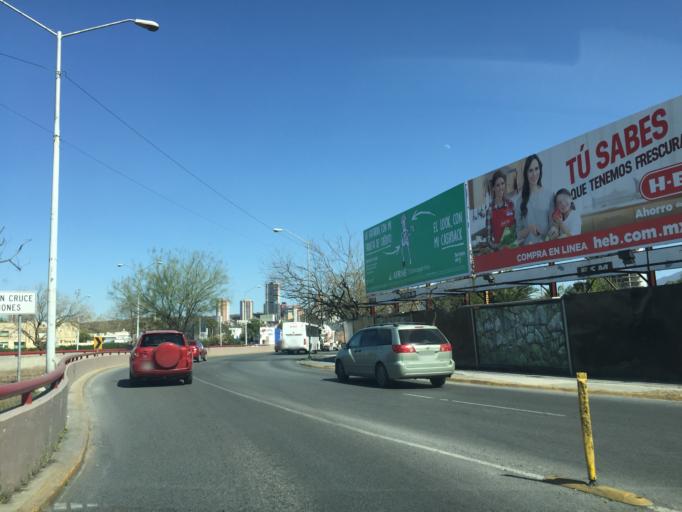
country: MX
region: Nuevo Leon
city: Garza Garcia
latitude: 25.6526
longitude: -100.3579
